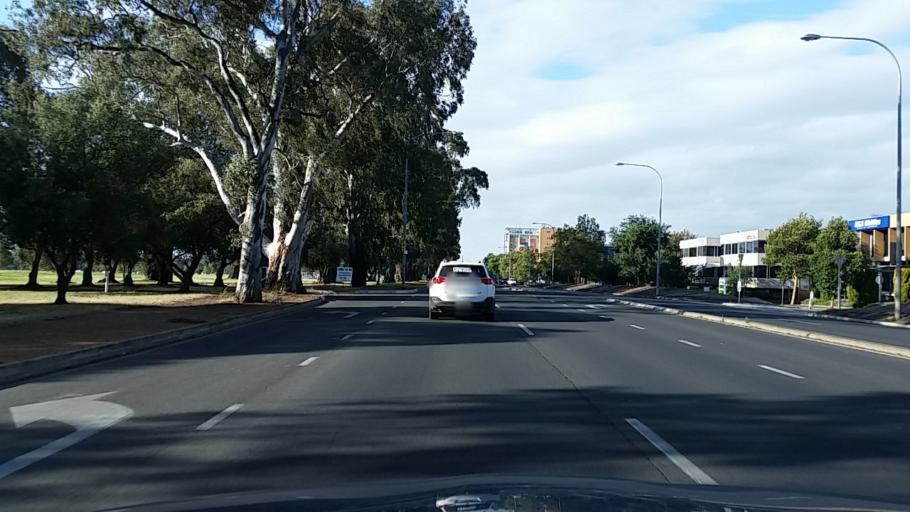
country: AU
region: South Australia
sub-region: Unley
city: Fullarton
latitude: -34.9371
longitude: 138.6241
